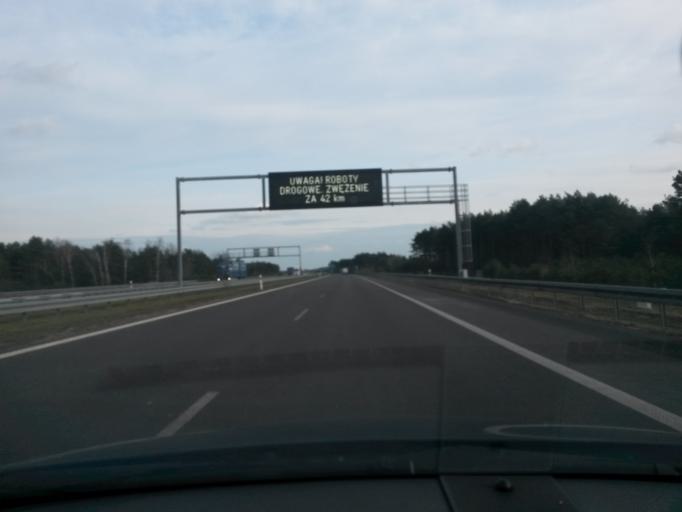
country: PL
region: Greater Poland Voivodeship
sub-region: Powiat kolski
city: Dabie
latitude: 52.0809
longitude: 18.7978
